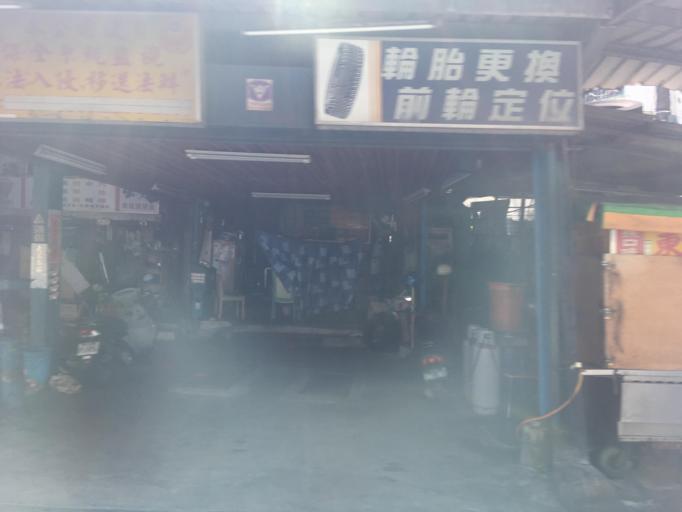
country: TW
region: Taipei
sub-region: Taipei
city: Banqiao
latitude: 25.0477
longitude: 121.4269
